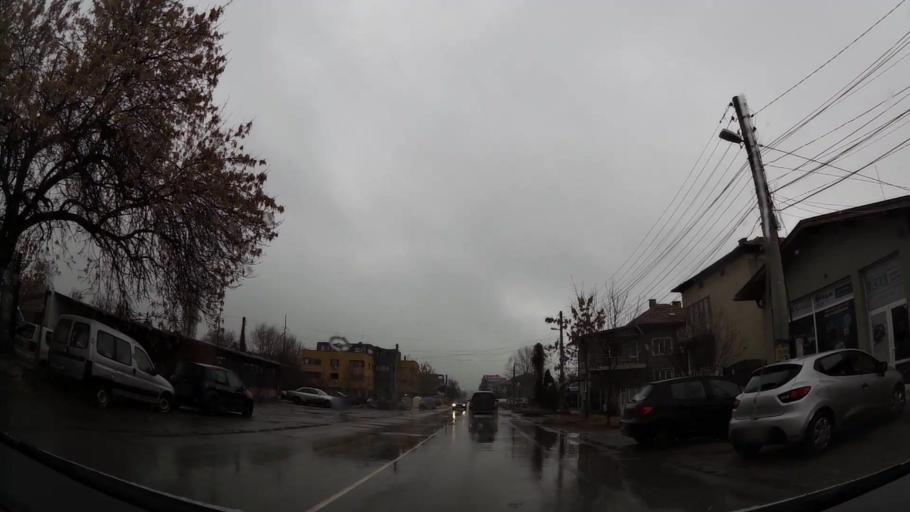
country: BG
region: Sofia-Capital
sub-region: Stolichna Obshtina
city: Sofia
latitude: 42.6346
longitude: 23.4099
